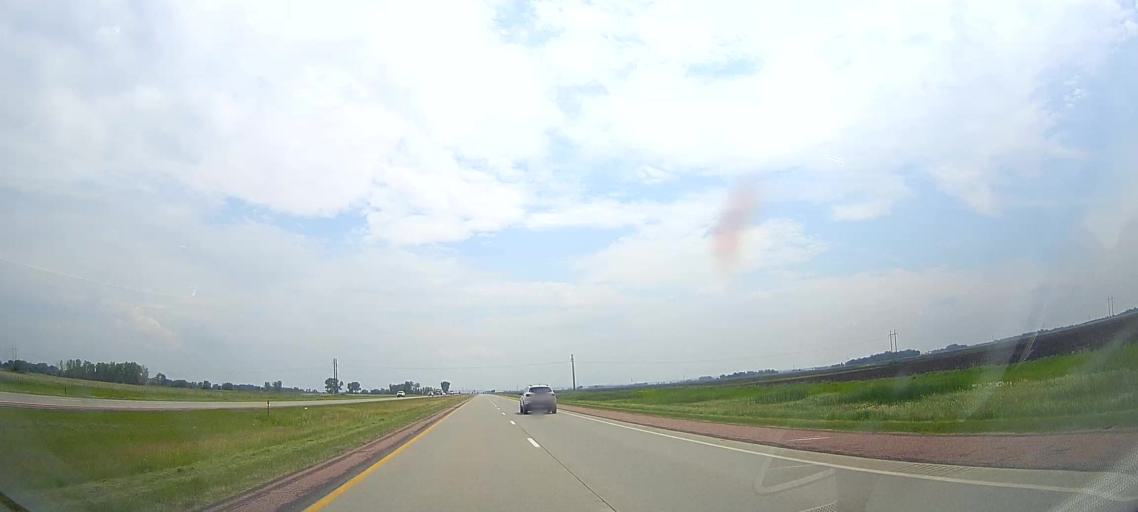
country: US
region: South Dakota
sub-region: Clay County
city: Vermillion
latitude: 42.8175
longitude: -96.7960
